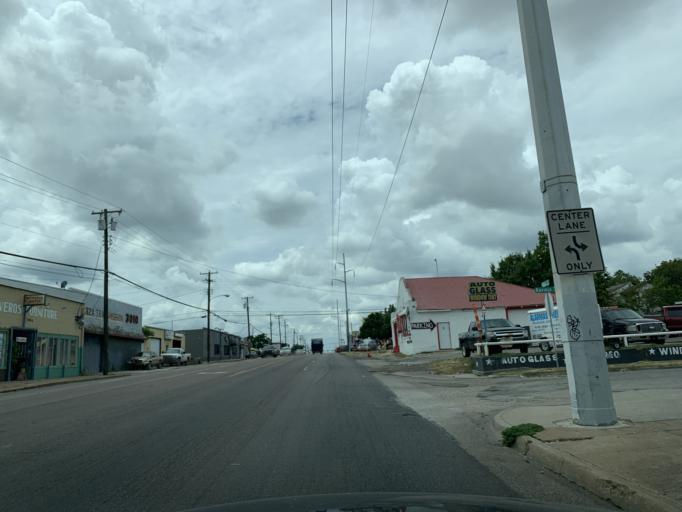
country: US
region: Texas
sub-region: Dallas County
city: Cockrell Hill
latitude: 32.7496
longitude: -96.8699
